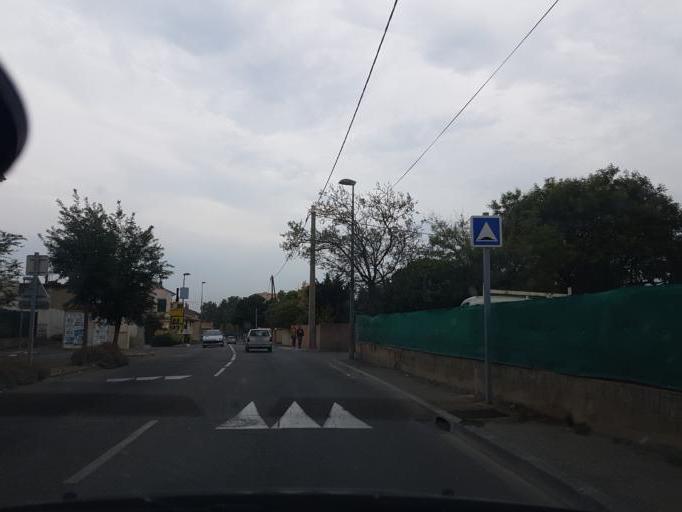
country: FR
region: Provence-Alpes-Cote d'Azur
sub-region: Departement du Vaucluse
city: Sorgues
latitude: 44.0073
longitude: 4.8812
